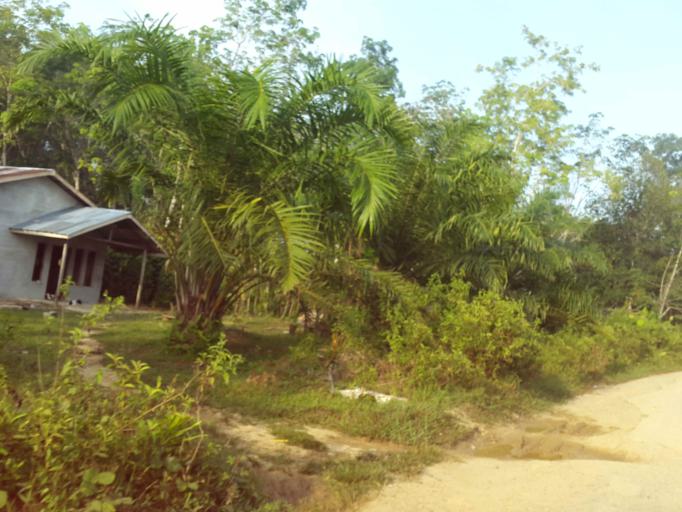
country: MY
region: Sarawak
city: Kuching
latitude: 0.8144
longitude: 110.4036
